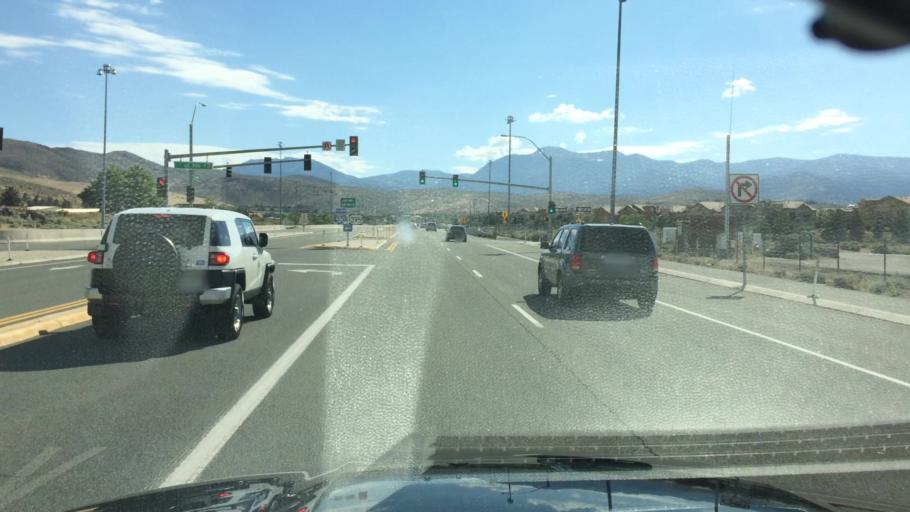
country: US
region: Nevada
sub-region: Washoe County
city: Sparks
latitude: 39.3966
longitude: -119.7591
